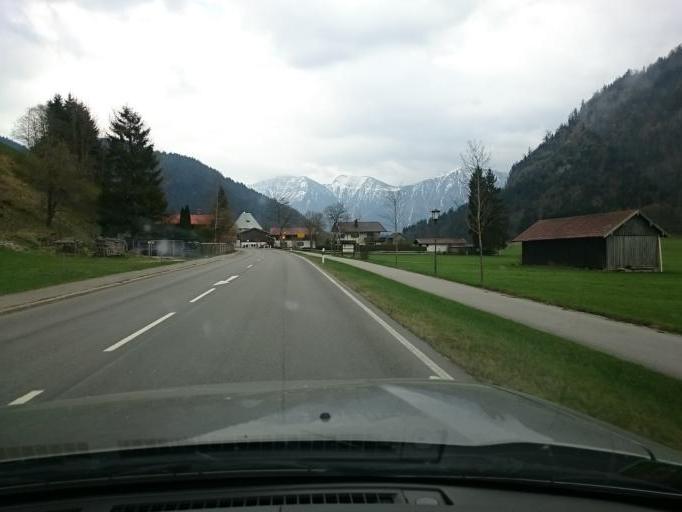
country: DE
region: Bavaria
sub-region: Upper Bavaria
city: Ettal
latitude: 47.5690
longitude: 11.0846
